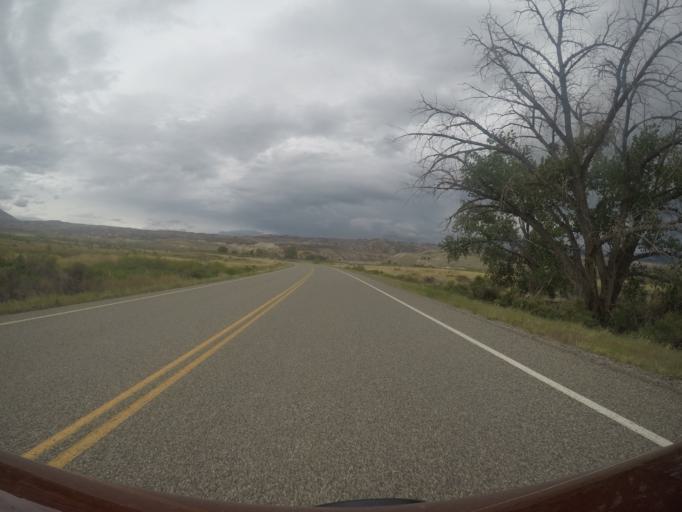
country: US
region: Wyoming
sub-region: Big Horn County
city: Lovell
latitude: 44.9651
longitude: -108.2753
